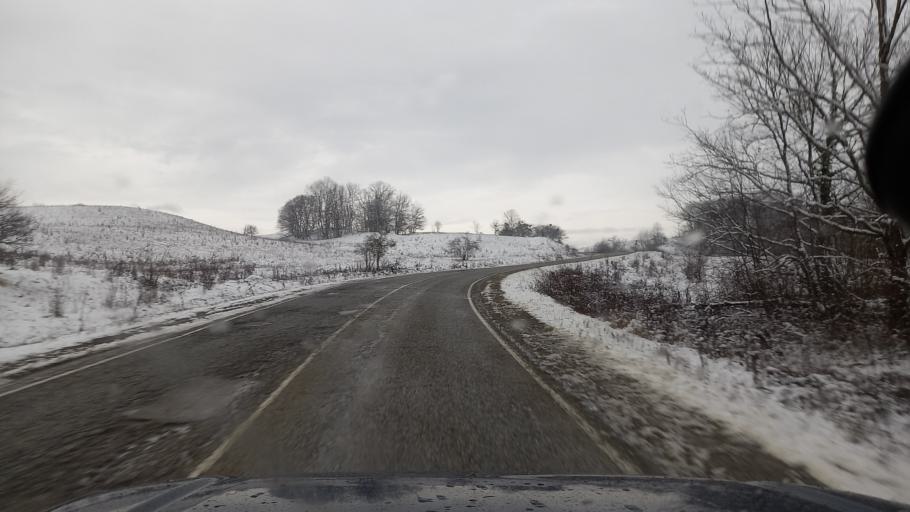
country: RU
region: Adygeya
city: Abadzekhskaya
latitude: 44.3487
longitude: 40.3322
